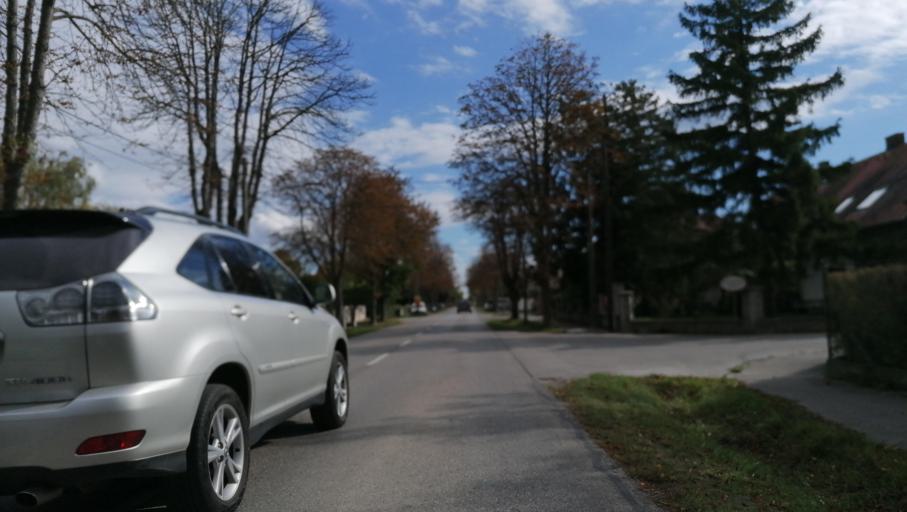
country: AT
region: Lower Austria
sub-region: Politischer Bezirk Baden
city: Teesdorf
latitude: 47.9799
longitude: 16.2738
